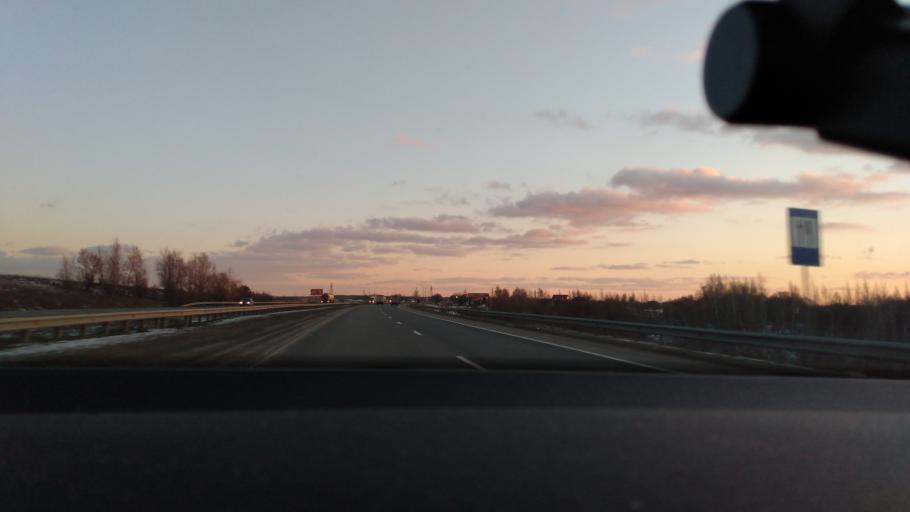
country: RU
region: Moskovskaya
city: Kolomna
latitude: 55.0980
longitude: 38.9019
